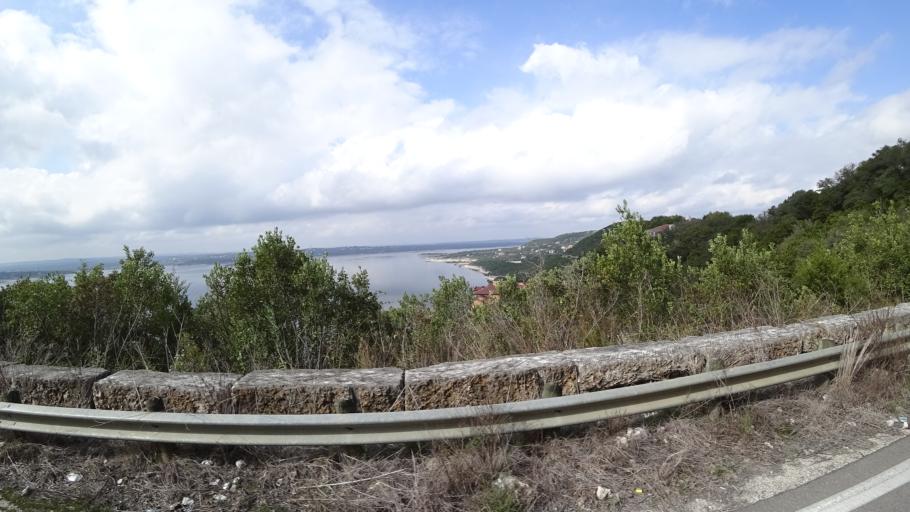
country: US
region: Texas
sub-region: Travis County
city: Hudson Bend
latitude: 30.4107
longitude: -97.8758
